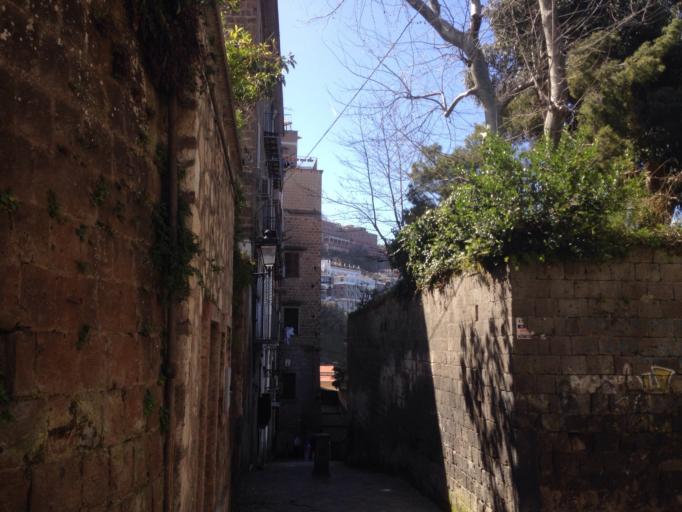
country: IT
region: Campania
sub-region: Provincia di Napoli
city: Sorrento
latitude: 40.6275
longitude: 14.3679
